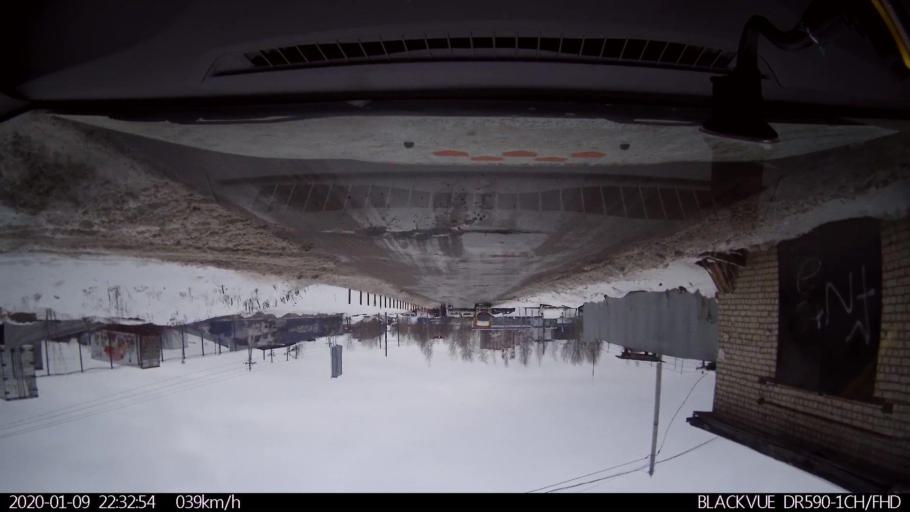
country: RU
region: Nizjnij Novgorod
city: Afonino
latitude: 56.2385
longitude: 44.0085
